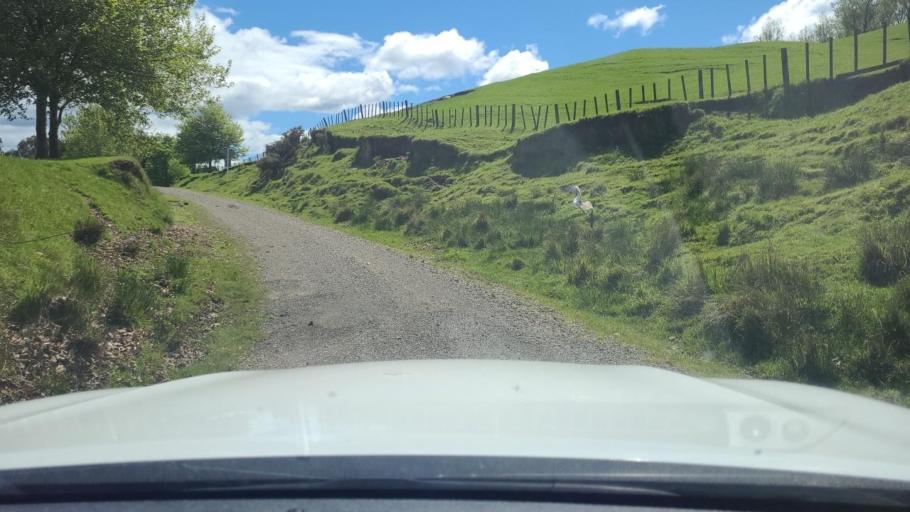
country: NZ
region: Hawke's Bay
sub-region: Napier City
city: Napier
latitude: -39.1708
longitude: 176.6604
